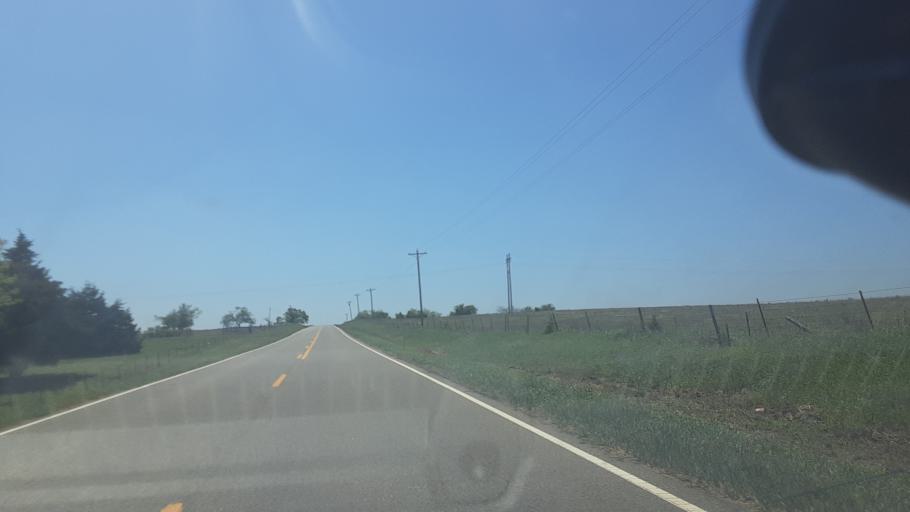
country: US
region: Oklahoma
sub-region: Logan County
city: Guthrie
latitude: 36.0230
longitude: -97.4076
